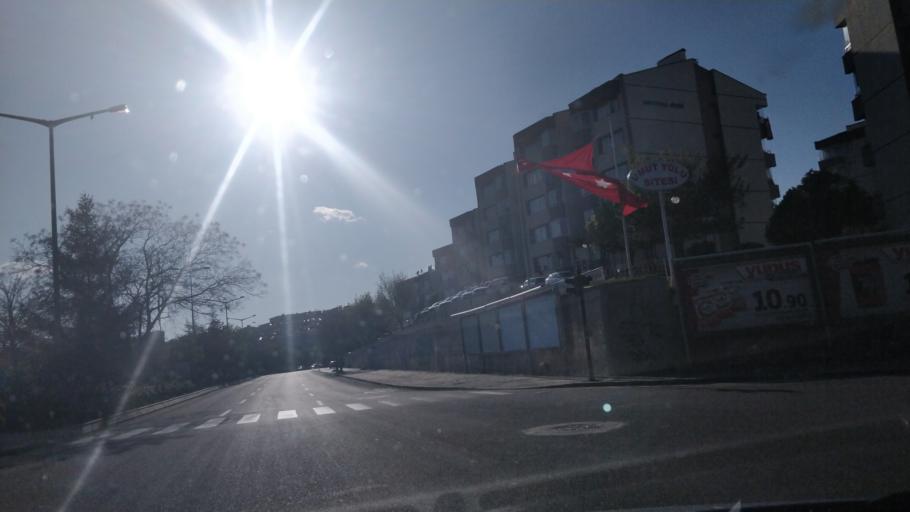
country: TR
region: Ankara
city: Batikent
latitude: 39.9580
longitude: 32.7236
